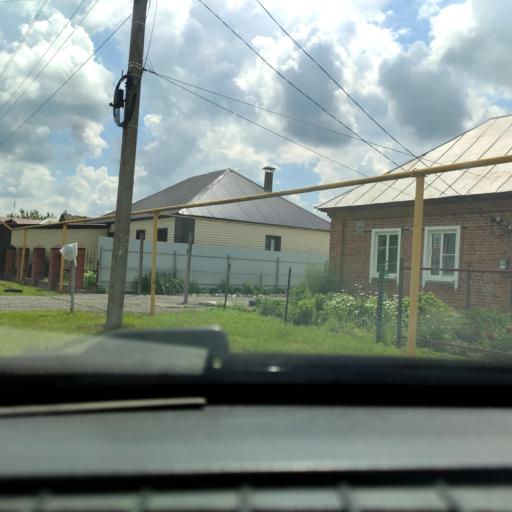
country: RU
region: Voronezj
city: Novaya Usman'
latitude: 51.6212
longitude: 39.3766
